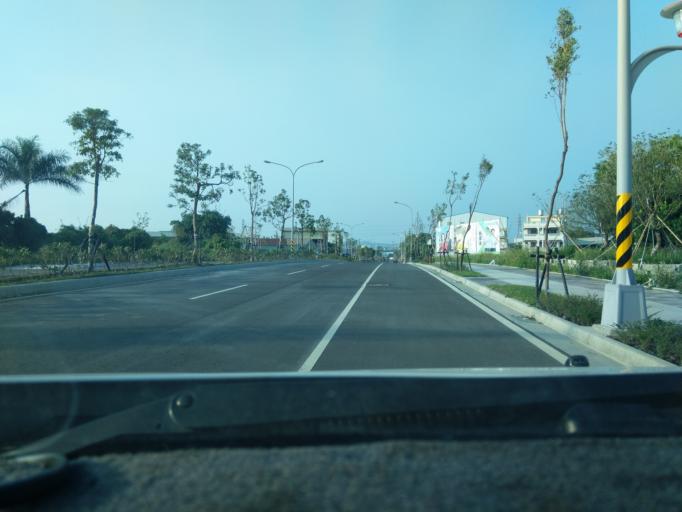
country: TW
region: Taiwan
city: Fengyuan
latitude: 24.2669
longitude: 120.7234
